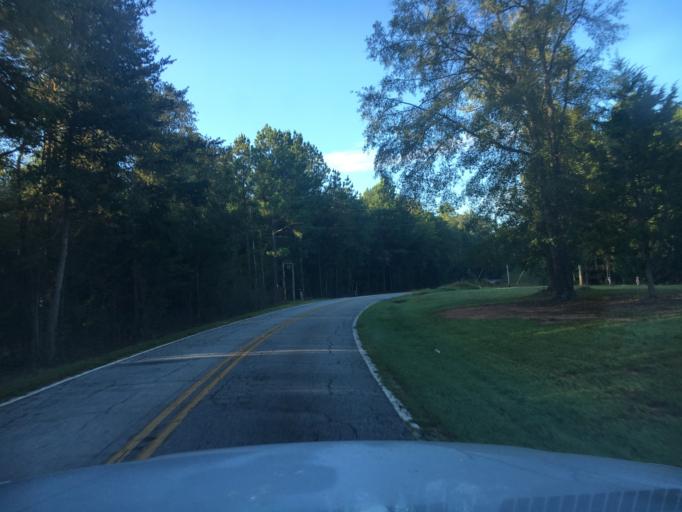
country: US
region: South Carolina
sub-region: Spartanburg County
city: Woodruff
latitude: 34.7651
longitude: -81.9609
